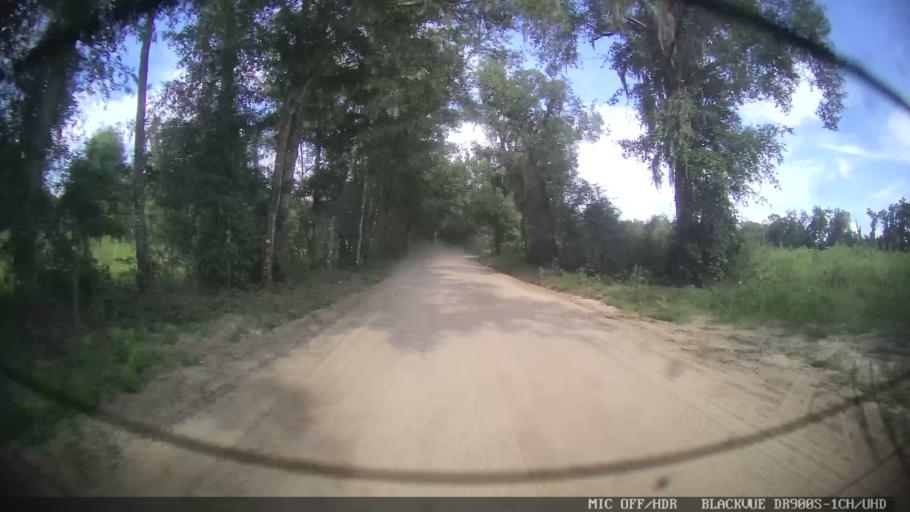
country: US
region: Georgia
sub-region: Lowndes County
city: Valdosta
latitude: 30.6205
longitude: -83.2422
